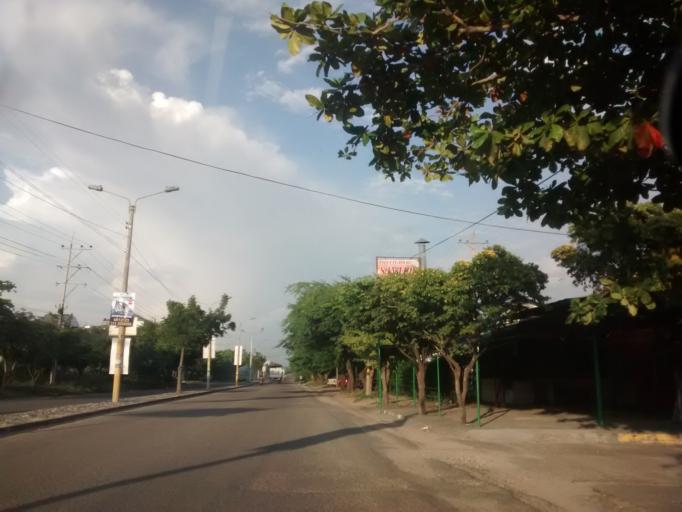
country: CO
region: Tolima
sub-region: Flandes
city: Flandes
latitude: 4.2980
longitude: -74.8209
